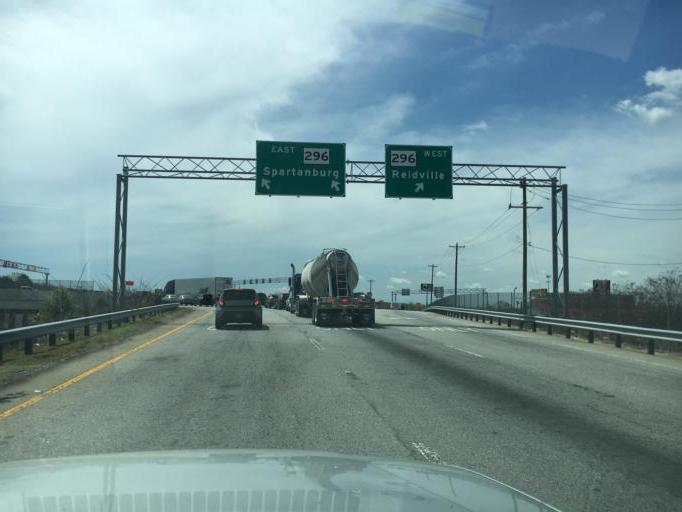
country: US
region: South Carolina
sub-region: Spartanburg County
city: Arcadia
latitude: 34.9233
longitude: -81.9891
